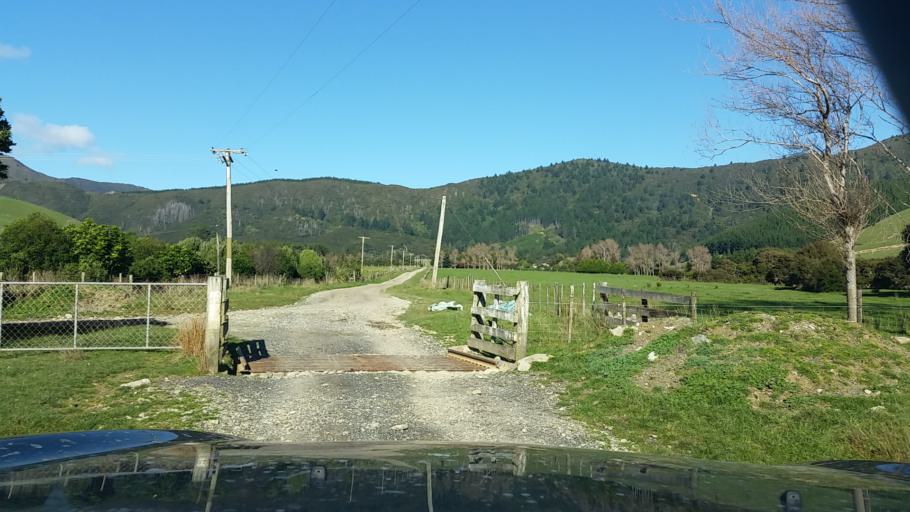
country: NZ
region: Marlborough
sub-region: Marlborough District
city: Picton
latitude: -41.1158
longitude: 174.0359
